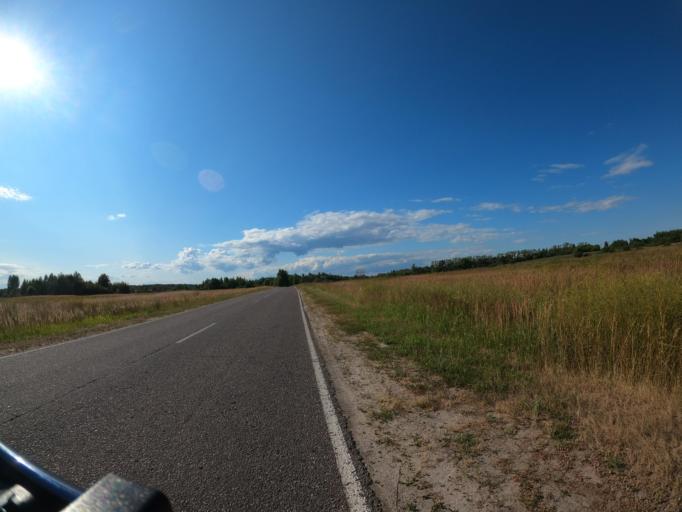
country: RU
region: Moskovskaya
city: Konobeyevo
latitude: 55.3997
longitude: 38.7123
